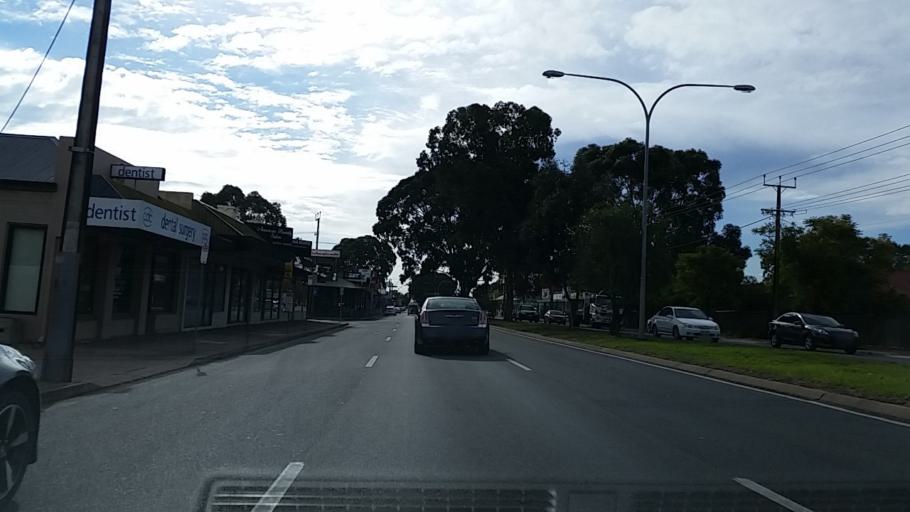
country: AU
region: South Australia
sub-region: Mitcham
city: Clapham
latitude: -34.9829
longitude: 138.5920
